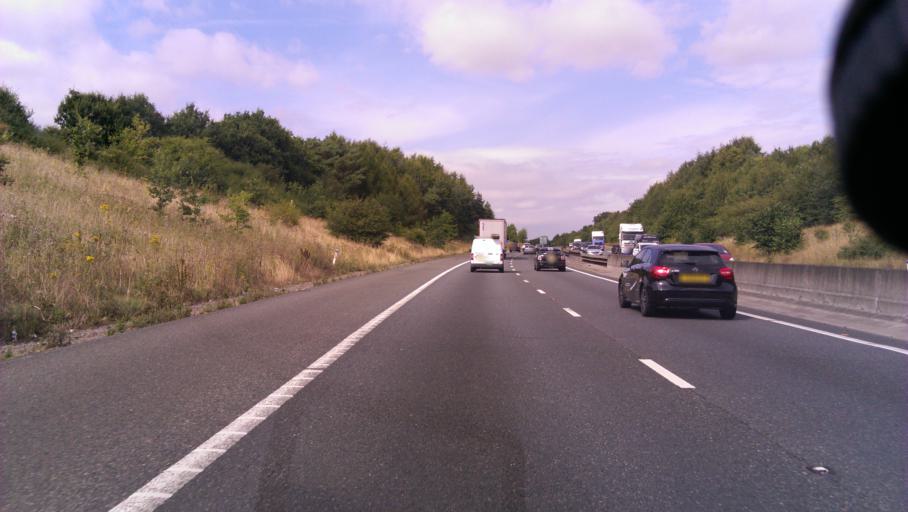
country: GB
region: England
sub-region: Essex
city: Elsenham
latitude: 51.9606
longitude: 0.2132
